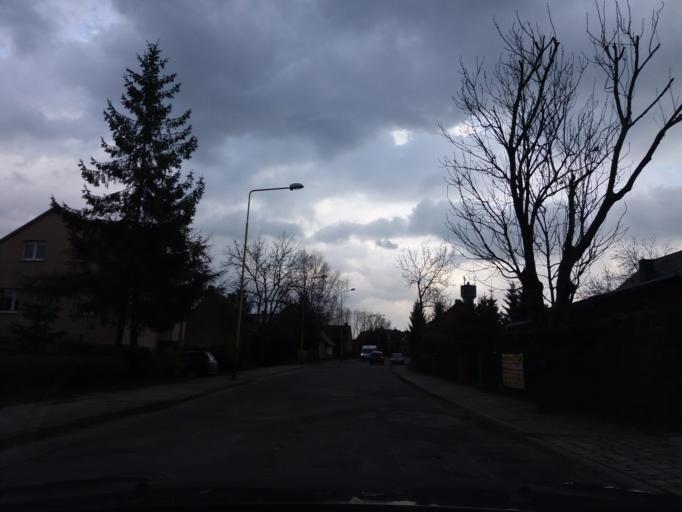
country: PL
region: West Pomeranian Voivodeship
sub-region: Powiat pyrzycki
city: Pyrzyce
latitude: 53.1394
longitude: 14.9066
